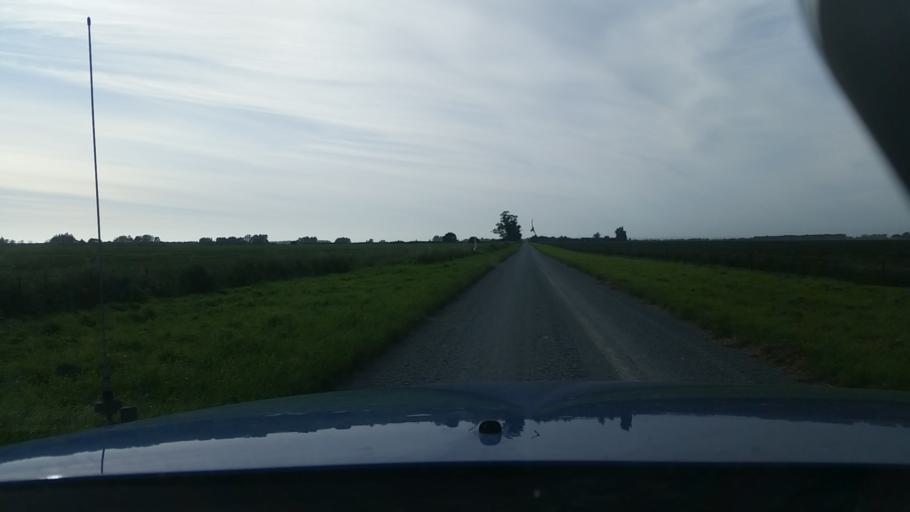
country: NZ
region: Canterbury
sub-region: Ashburton District
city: Tinwald
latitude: -44.0001
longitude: 171.7993
